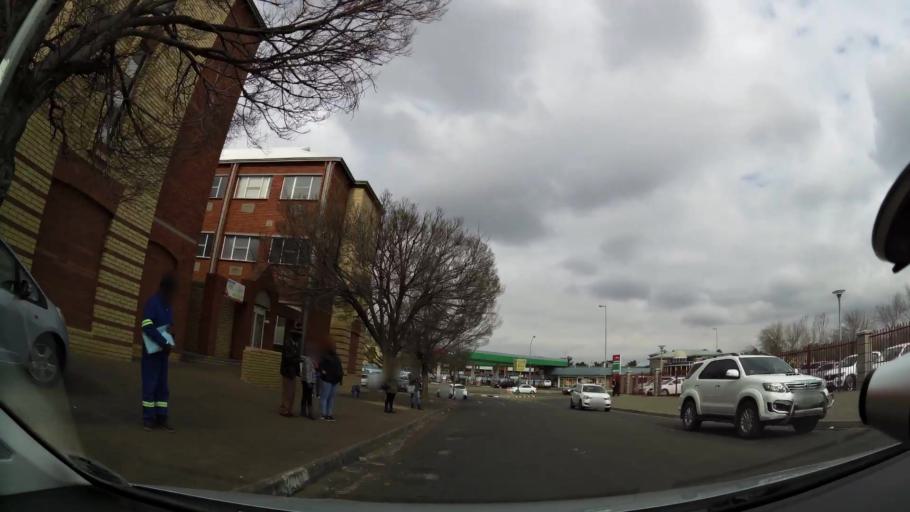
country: ZA
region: Orange Free State
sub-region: Mangaung Metropolitan Municipality
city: Bloemfontein
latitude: -29.1095
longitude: 26.2049
